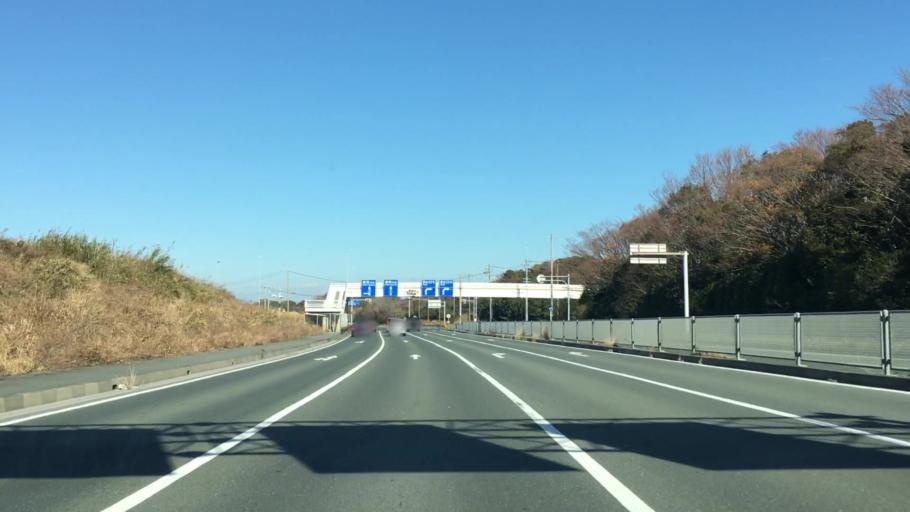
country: JP
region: Aichi
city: Tahara
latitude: 34.6968
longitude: 137.3247
